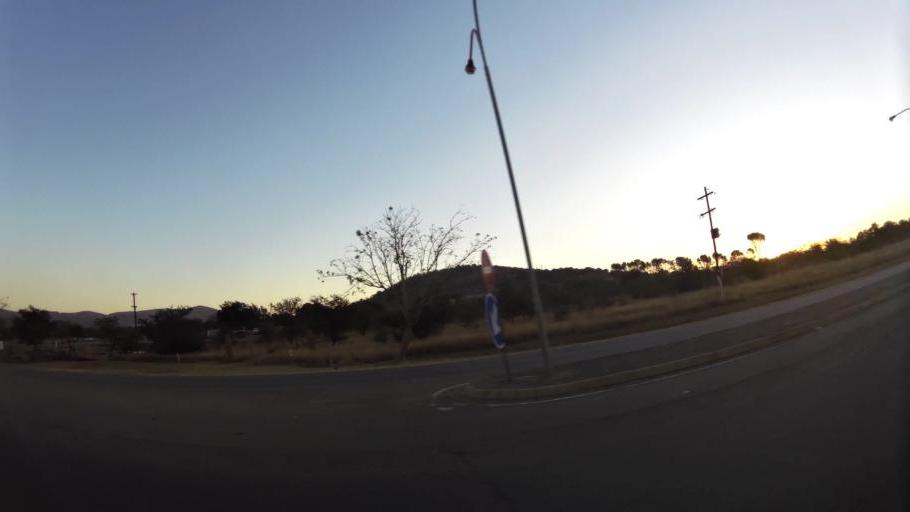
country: ZA
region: North-West
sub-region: Bojanala Platinum District Municipality
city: Rustenburg
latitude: -25.6265
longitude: 27.1861
